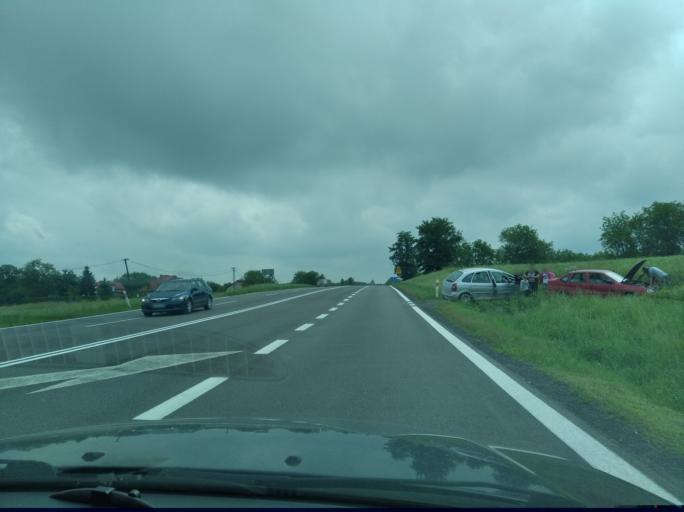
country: PL
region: Subcarpathian Voivodeship
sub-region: Powiat przeworski
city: Rozborz
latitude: 50.0454
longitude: 22.5444
